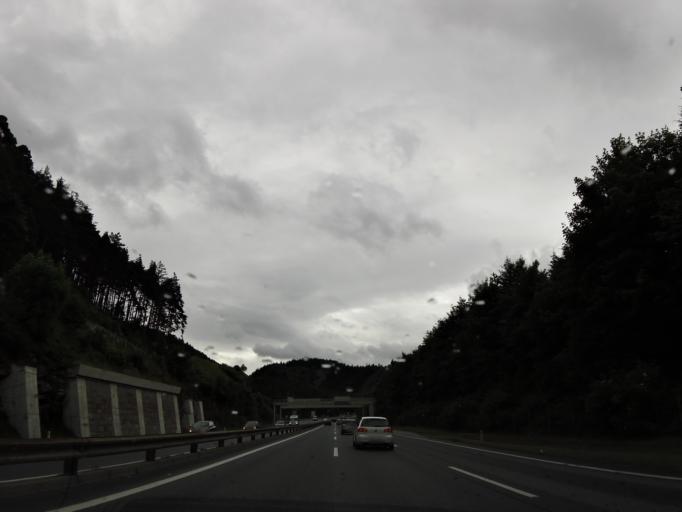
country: AT
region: Tyrol
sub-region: Politischer Bezirk Innsbruck Land
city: Mutters
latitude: 47.2331
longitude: 11.3926
